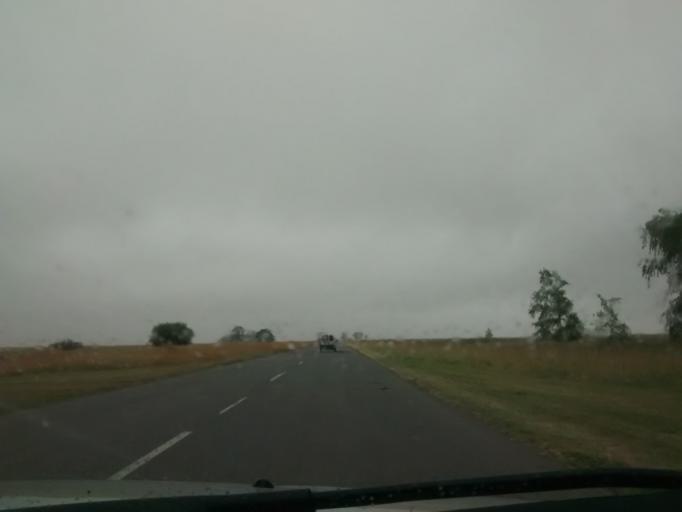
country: AR
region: Buenos Aires
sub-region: Partido de Ayacucho
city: Ayacucho
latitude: -37.4790
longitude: -58.4789
